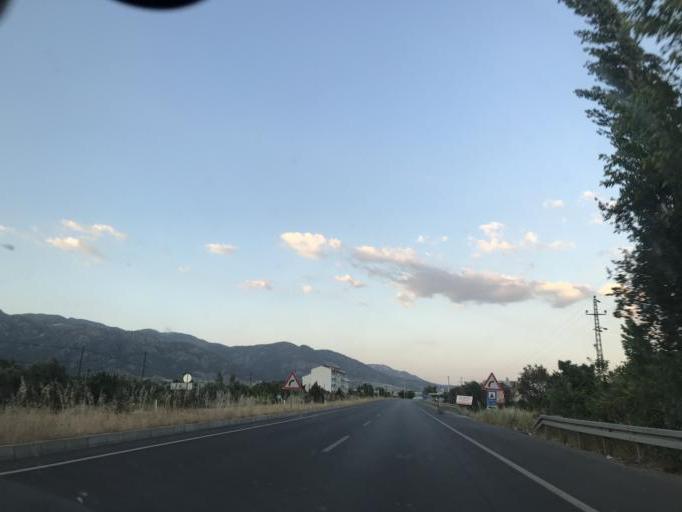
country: TR
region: Aydin
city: Buharkent
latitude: 37.9627
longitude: 28.7284
